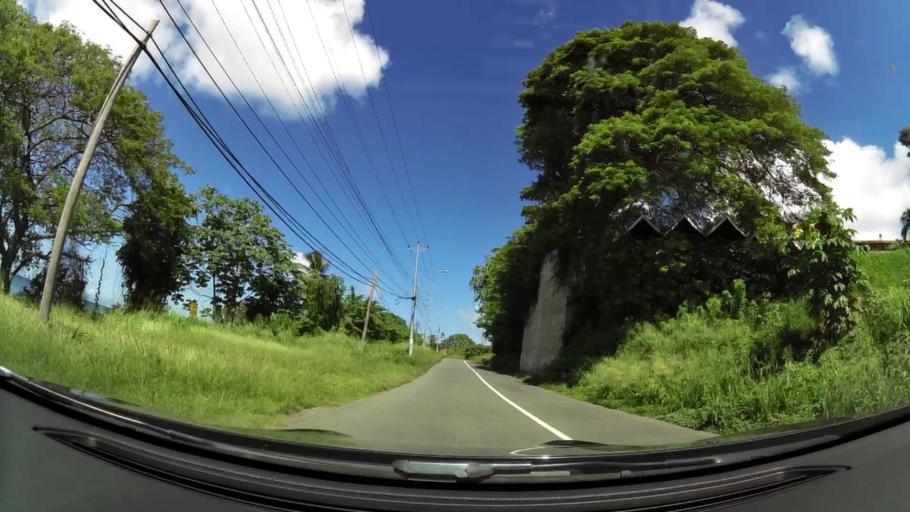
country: TT
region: Tobago
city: Scarborough
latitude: 11.1888
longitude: -60.7958
